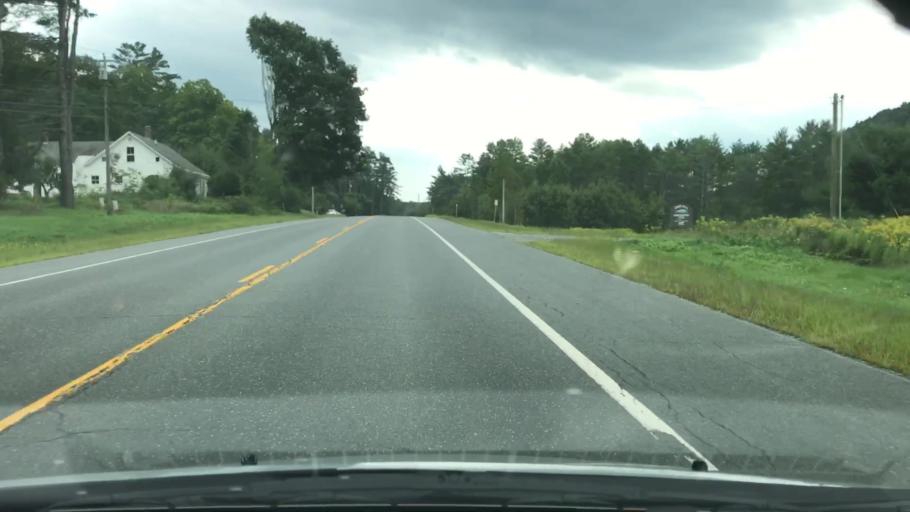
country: US
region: New Hampshire
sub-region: Grafton County
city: Lyme
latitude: 43.7964
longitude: -72.1695
